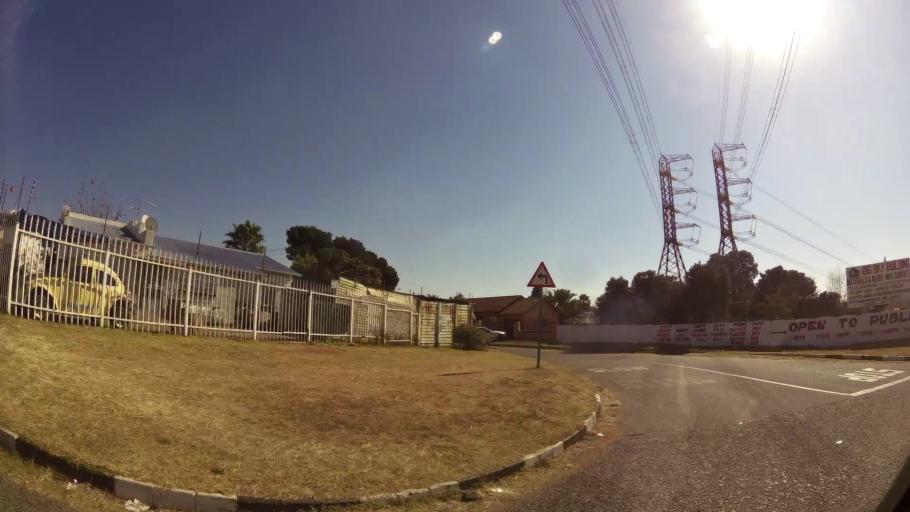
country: ZA
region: Gauteng
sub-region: City of Johannesburg Metropolitan Municipality
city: Johannesburg
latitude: -26.2547
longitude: 28.0954
